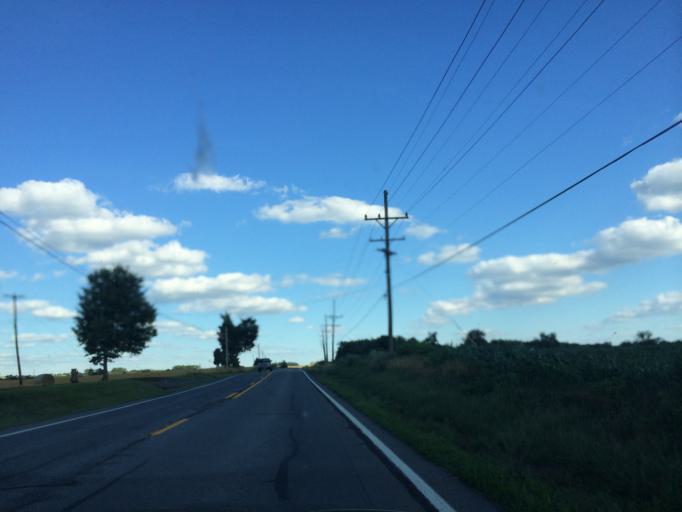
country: US
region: Maryland
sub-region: Frederick County
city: Woodsboro
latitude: 39.5719
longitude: -77.3610
